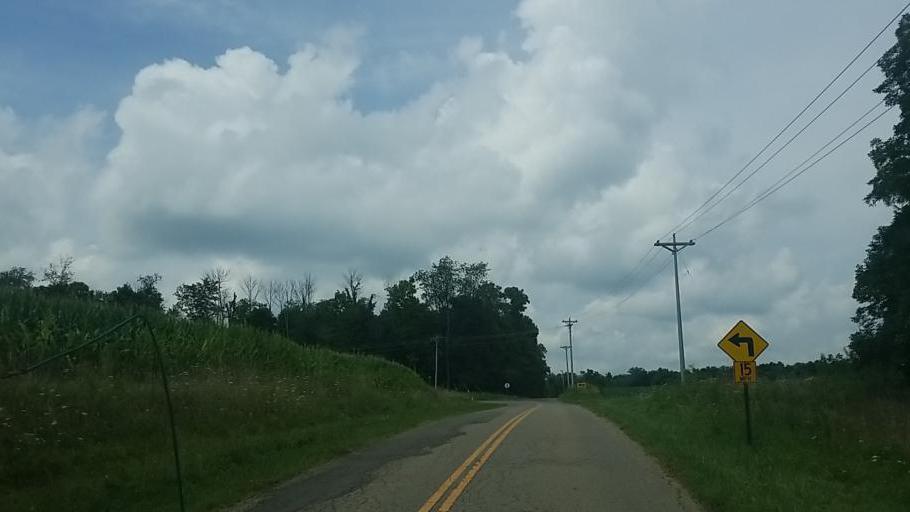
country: US
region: Ohio
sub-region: Knox County
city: Gambier
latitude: 40.3220
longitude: -82.4289
